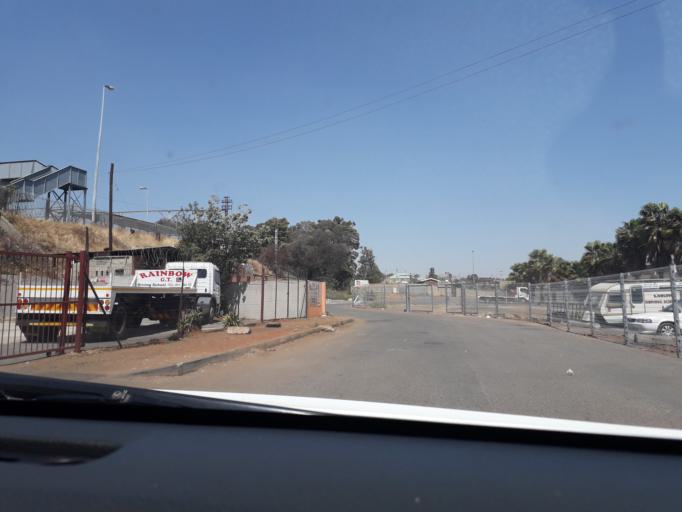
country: ZA
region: Gauteng
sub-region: City of Johannesburg Metropolitan Municipality
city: Modderfontein
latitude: -26.1086
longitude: 28.2263
